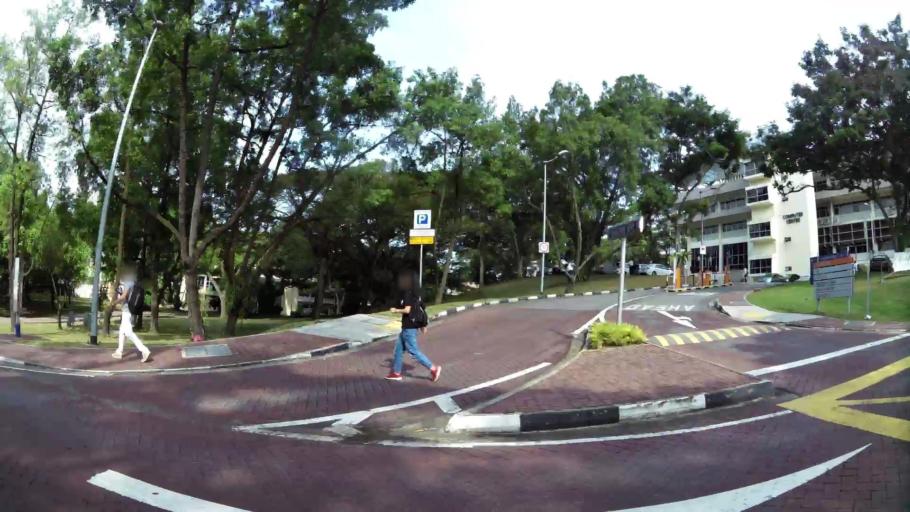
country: SG
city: Singapore
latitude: 1.2969
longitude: 103.7725
